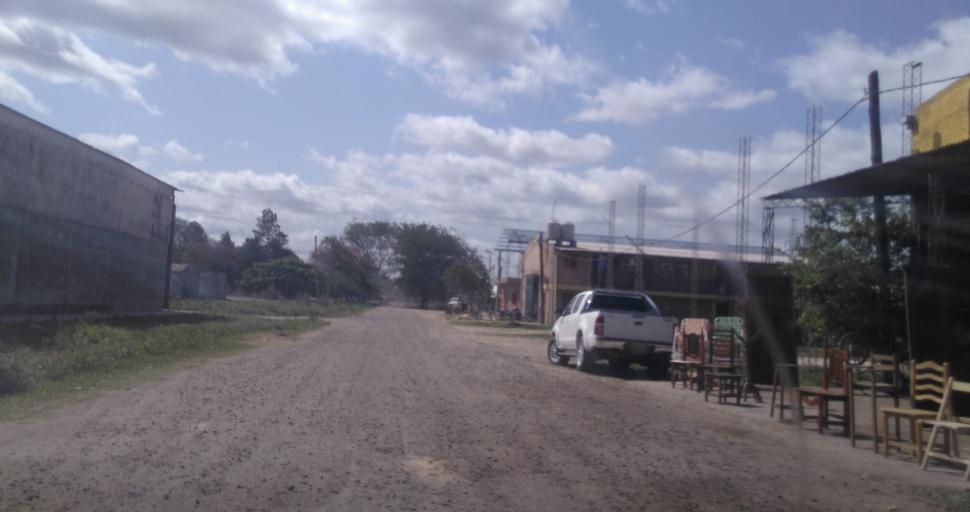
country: AR
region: Chaco
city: Fontana
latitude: -27.4302
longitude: -59.0241
